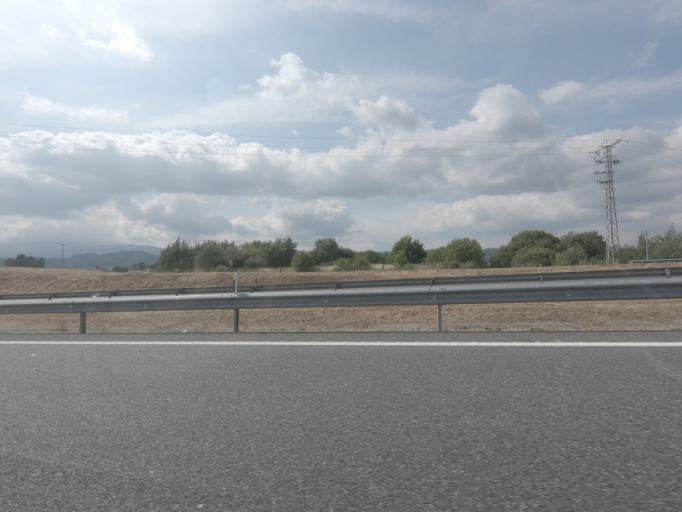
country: ES
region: Galicia
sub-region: Provincia de Ourense
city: Beade
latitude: 42.3064
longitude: -8.1197
